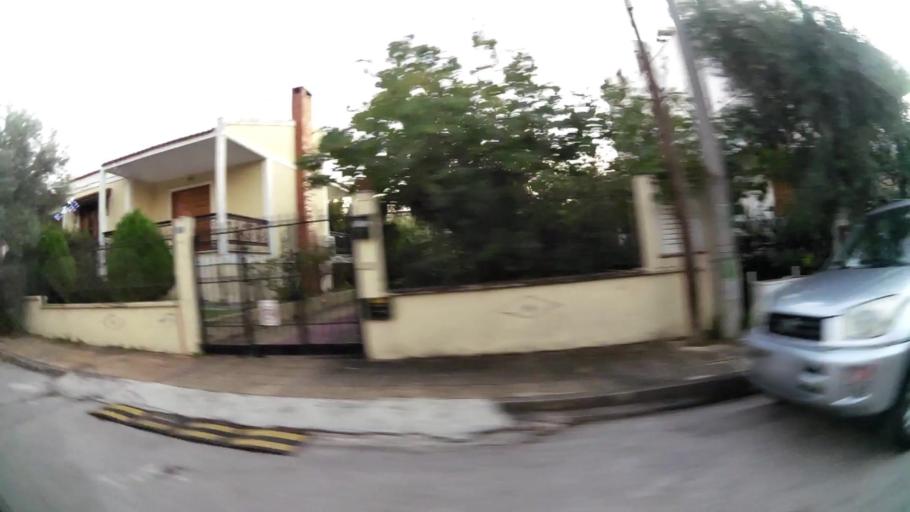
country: GR
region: Attica
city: Pefki
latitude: 38.0668
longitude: 23.8005
